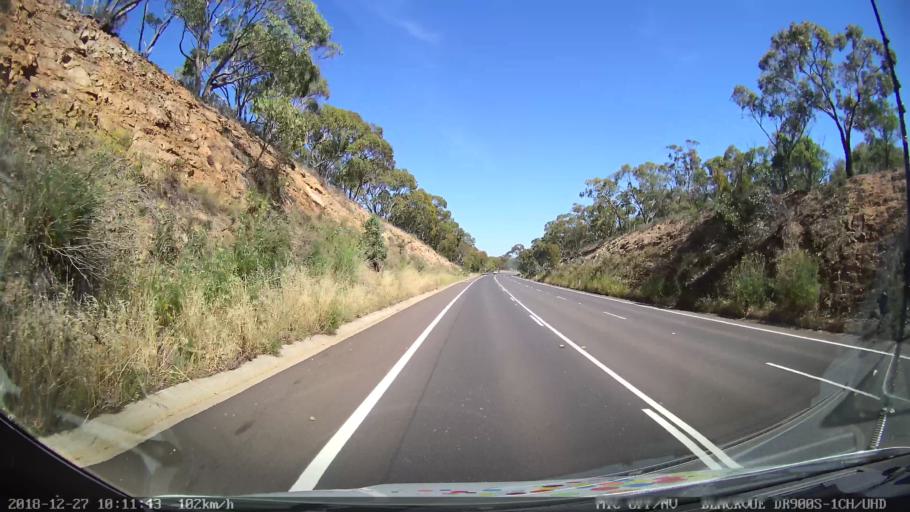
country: AU
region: New South Wales
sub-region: Bathurst Regional
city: Kelso
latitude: -33.4503
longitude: 149.7698
